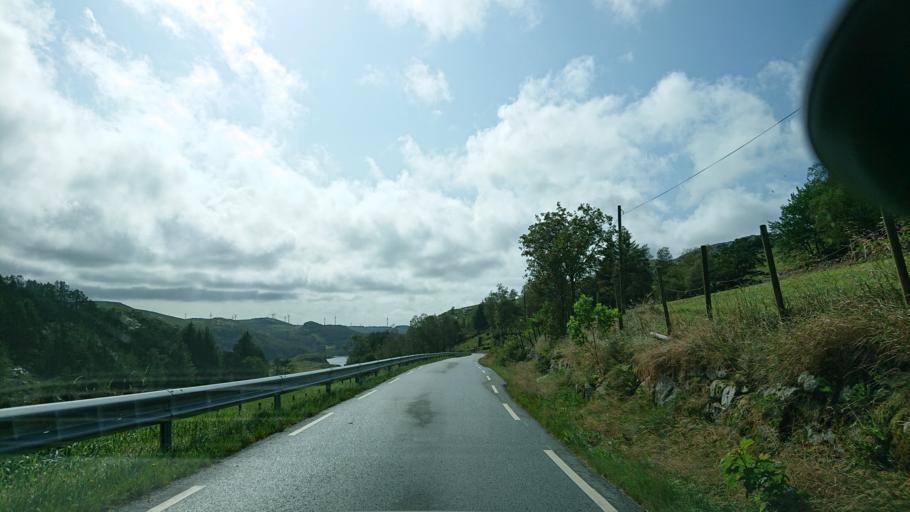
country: NO
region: Rogaland
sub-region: Gjesdal
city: Algard
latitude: 58.6811
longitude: 5.8559
